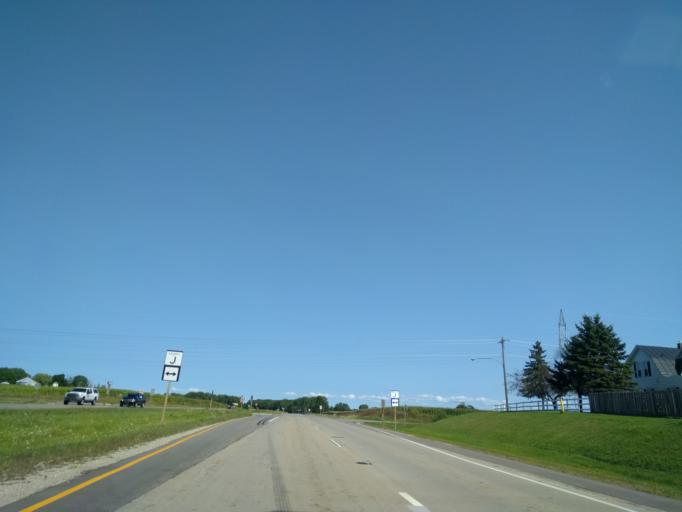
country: US
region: Wisconsin
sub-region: Oconto County
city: Oconto
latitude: 44.8005
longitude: -87.9996
